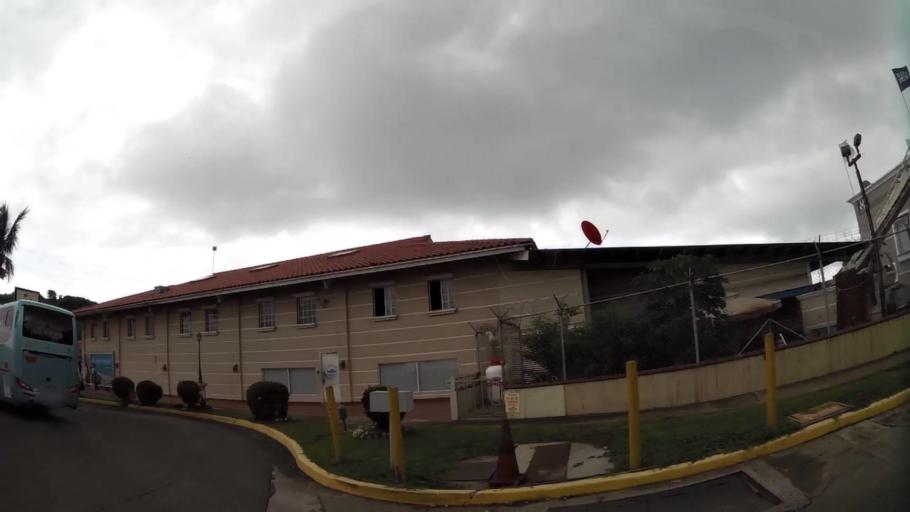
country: PA
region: Panama
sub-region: Distrito de Panama
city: Ancon
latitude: 8.9102
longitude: -79.5217
